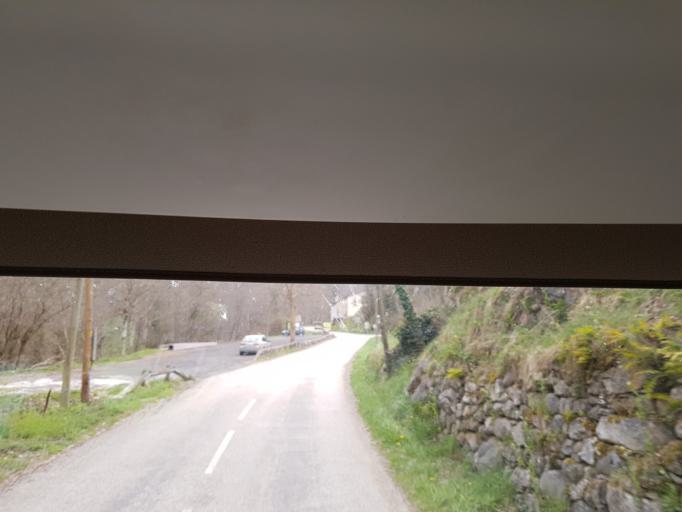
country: FR
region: Languedoc-Roussillon
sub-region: Departement de l'Aude
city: Quillan
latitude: 42.7359
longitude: 2.0859
